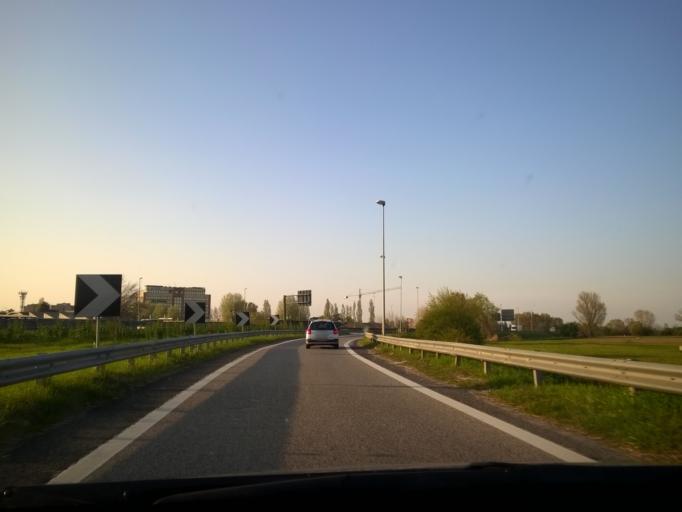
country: IT
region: Emilia-Romagna
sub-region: Provincia di Bologna
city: Progresso
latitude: 44.5336
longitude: 11.3626
